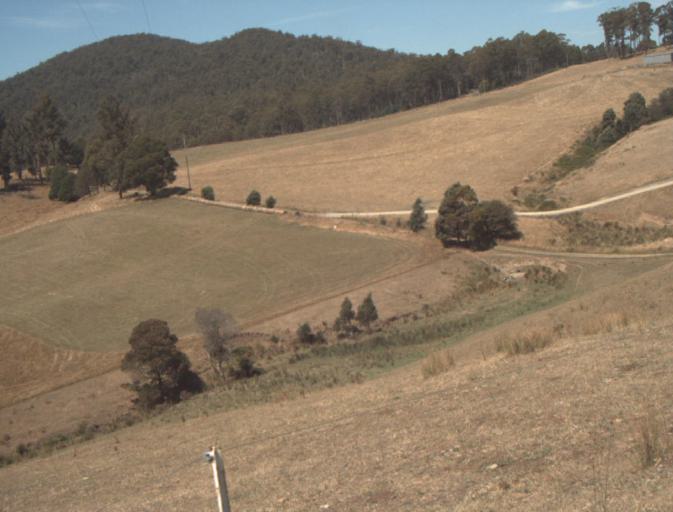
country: AU
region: Tasmania
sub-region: Launceston
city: Mayfield
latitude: -41.2703
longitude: 147.1224
